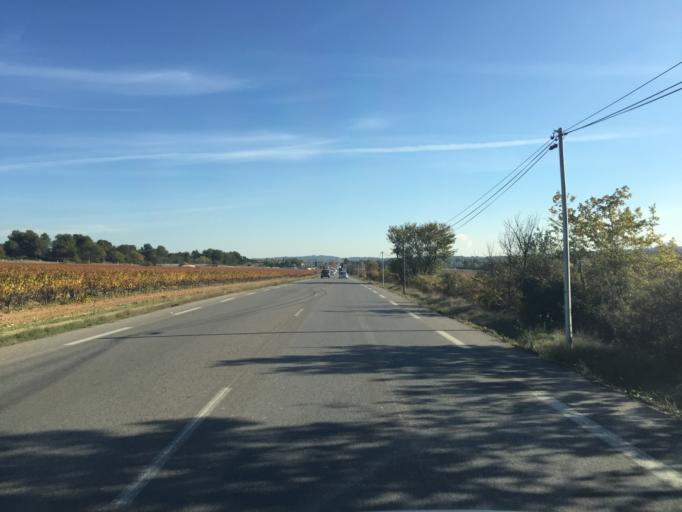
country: FR
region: Provence-Alpes-Cote d'Azur
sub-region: Departement des Bouches-du-Rhone
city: Eguilles
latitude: 43.5906
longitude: 5.3620
